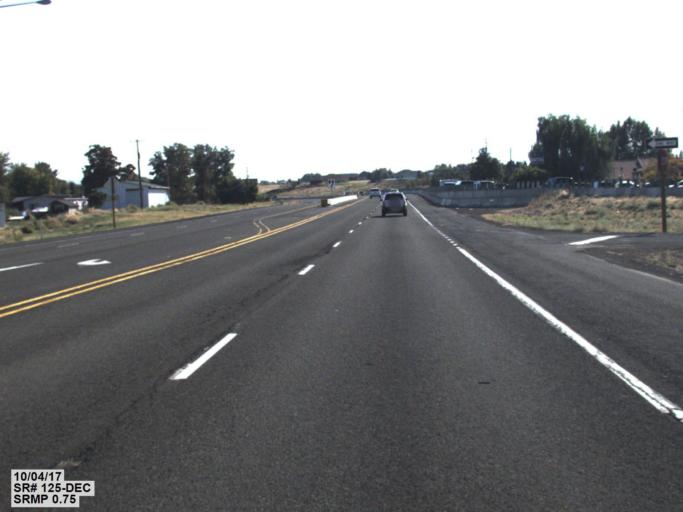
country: US
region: Washington
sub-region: Walla Walla County
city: College Place
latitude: 46.0112
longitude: -118.3898
